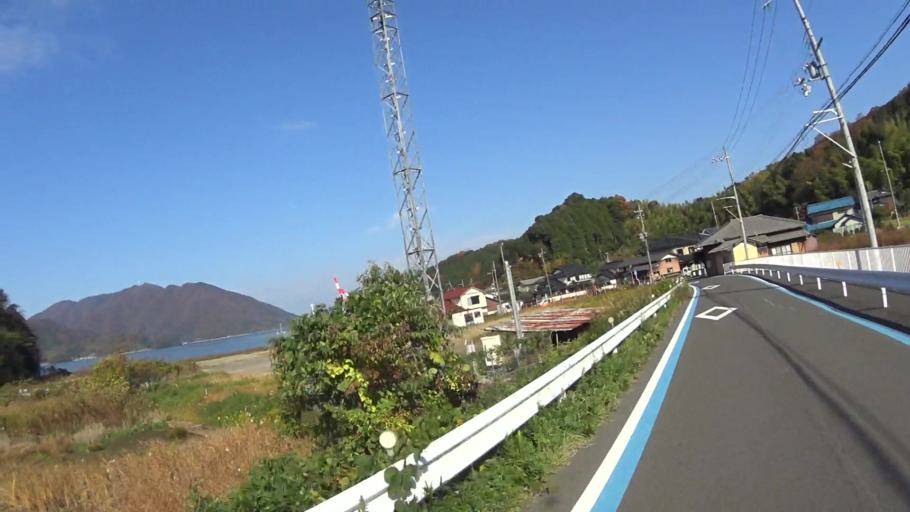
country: JP
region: Kyoto
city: Maizuru
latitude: 35.4631
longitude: 135.3293
